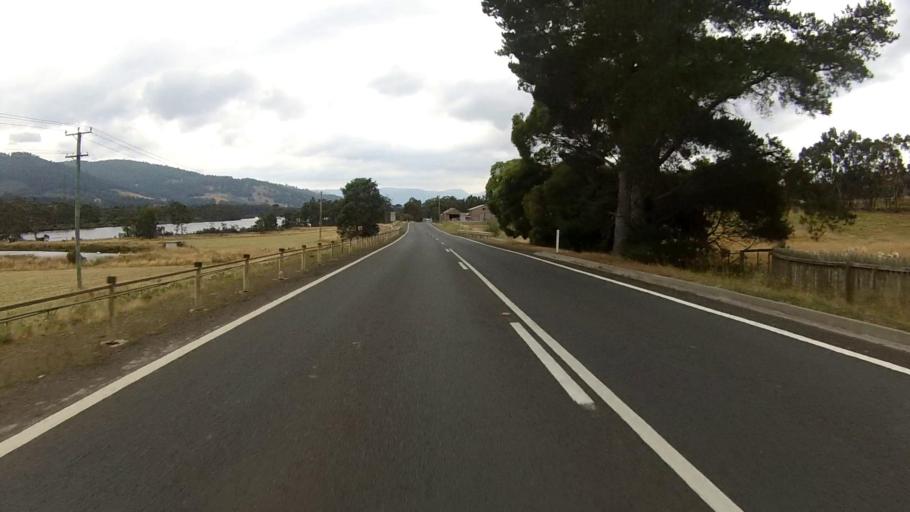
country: AU
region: Tasmania
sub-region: Huon Valley
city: Franklin
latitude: -43.0846
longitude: 147.0301
